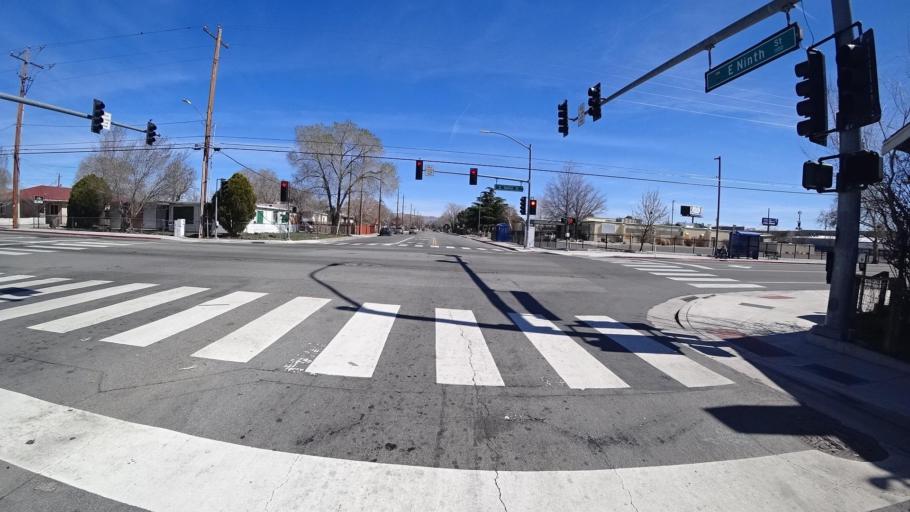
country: US
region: Nevada
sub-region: Washoe County
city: Reno
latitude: 39.5385
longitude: -119.7988
